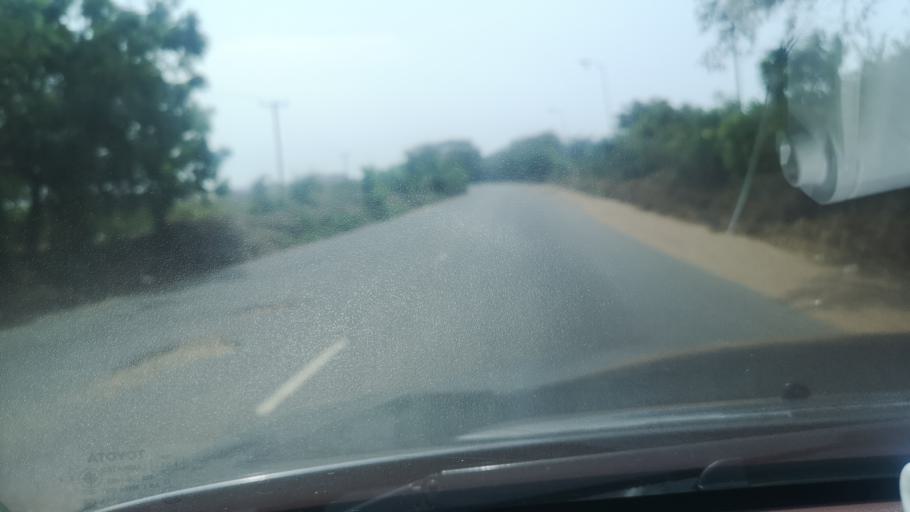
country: GH
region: Greater Accra
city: Nungua
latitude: 5.6140
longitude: -0.0572
